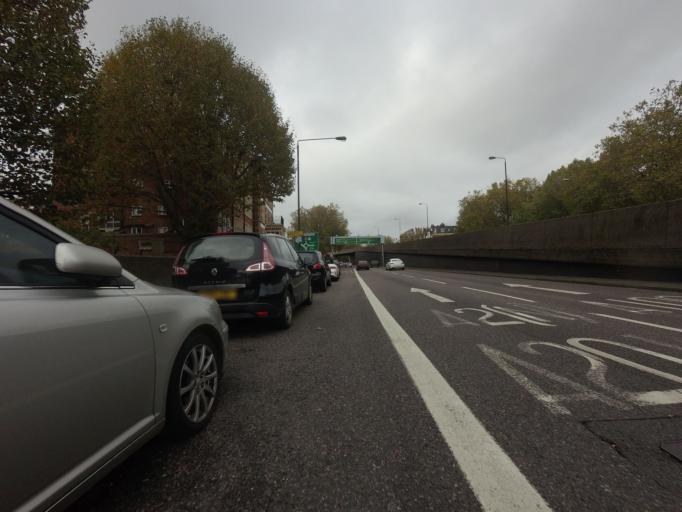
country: GB
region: England
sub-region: Greater London
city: Camberwell
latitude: 51.4928
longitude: -0.0839
